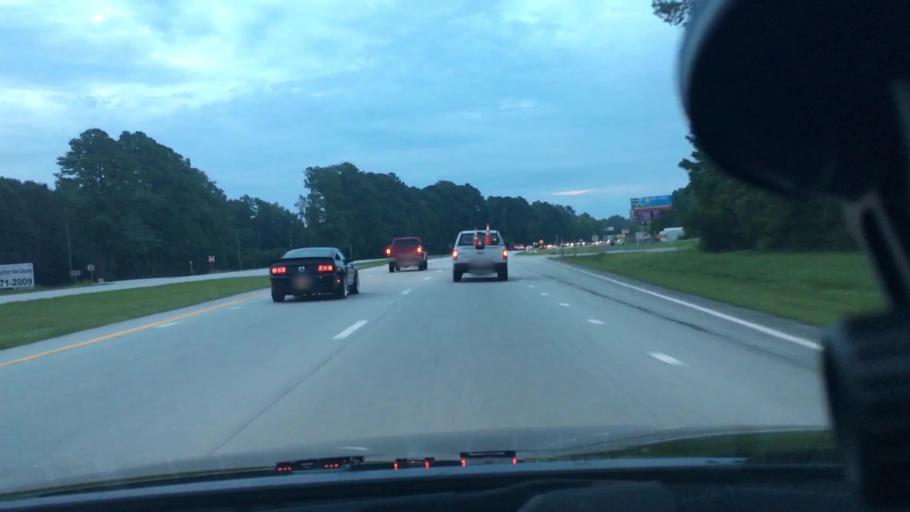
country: US
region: North Carolina
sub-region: Craven County
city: Neuse Forest
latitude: 34.9596
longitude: -76.9526
